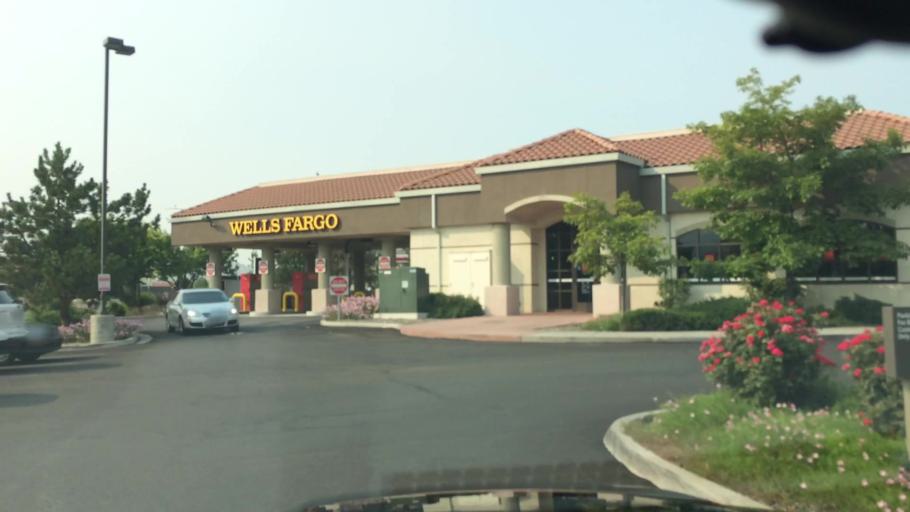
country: US
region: Nevada
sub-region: Washoe County
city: Sparks
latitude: 39.4391
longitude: -119.7618
